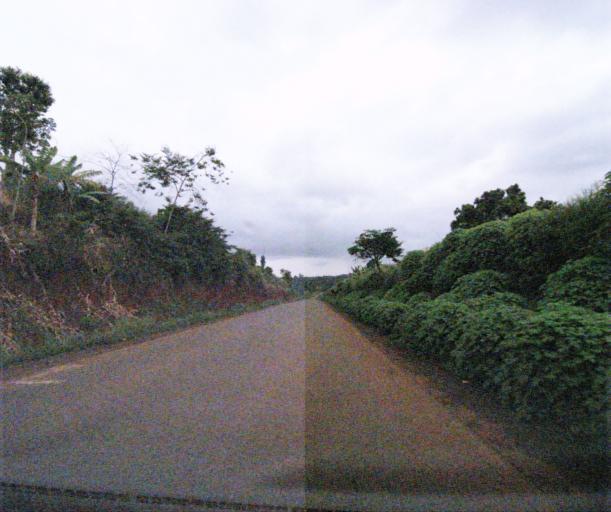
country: CM
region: West
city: Bansoa
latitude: 5.4962
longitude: 10.2292
